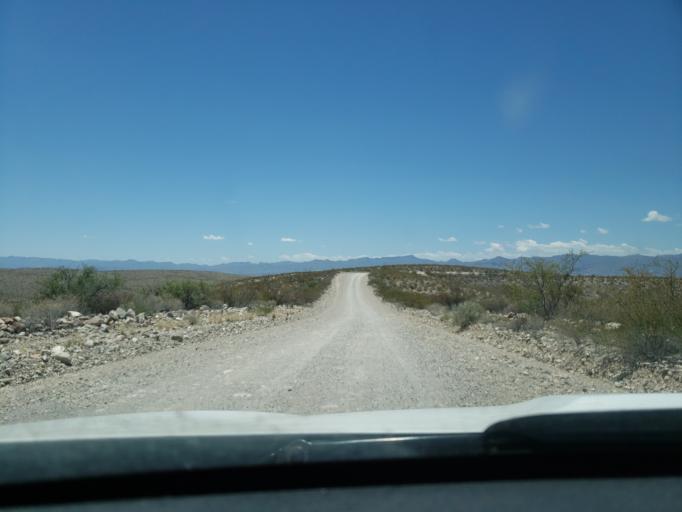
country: MX
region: Chihuahua
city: Ojinaga
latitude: 29.9980
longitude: -104.5760
